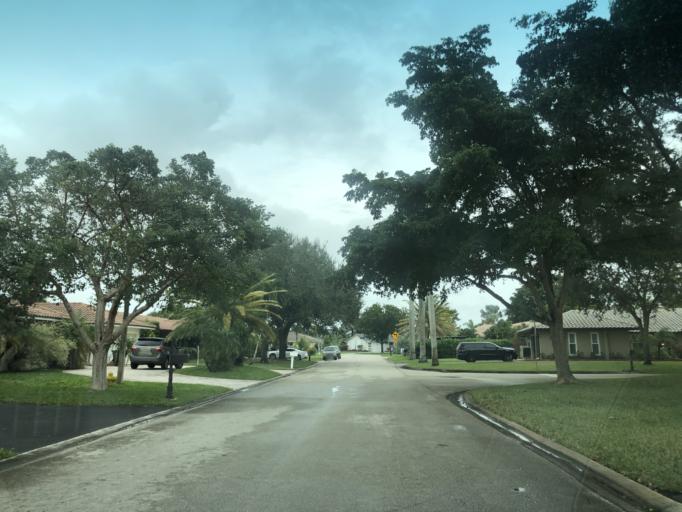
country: US
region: Florida
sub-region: Broward County
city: North Lauderdale
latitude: 26.2391
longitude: -80.2359
